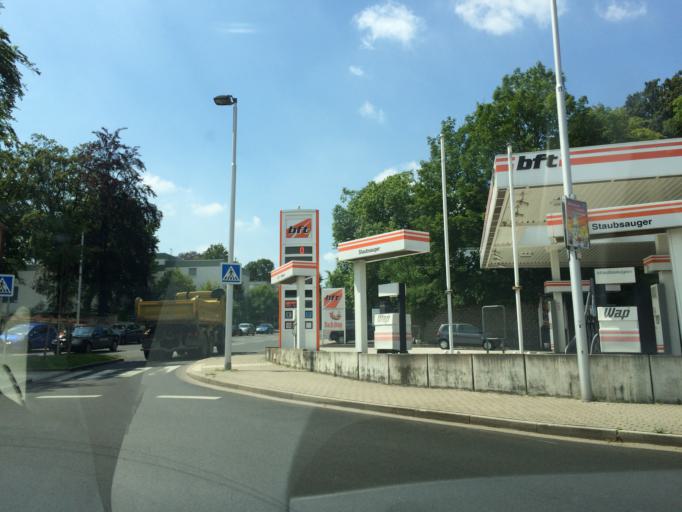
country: DE
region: North Rhine-Westphalia
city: Iserlohn
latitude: 51.3725
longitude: 7.7169
